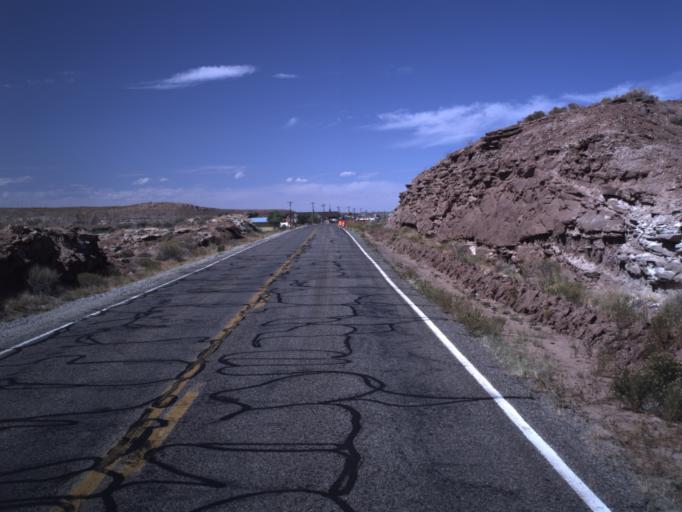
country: US
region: Utah
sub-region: San Juan County
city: Blanding
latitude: 37.2578
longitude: -109.2927
